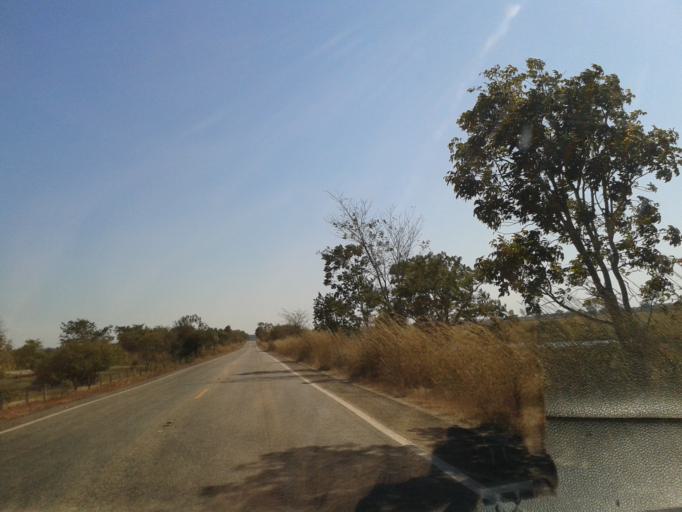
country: BR
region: Goias
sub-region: Mozarlandia
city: Mozarlandia
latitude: -14.5104
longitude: -50.4851
